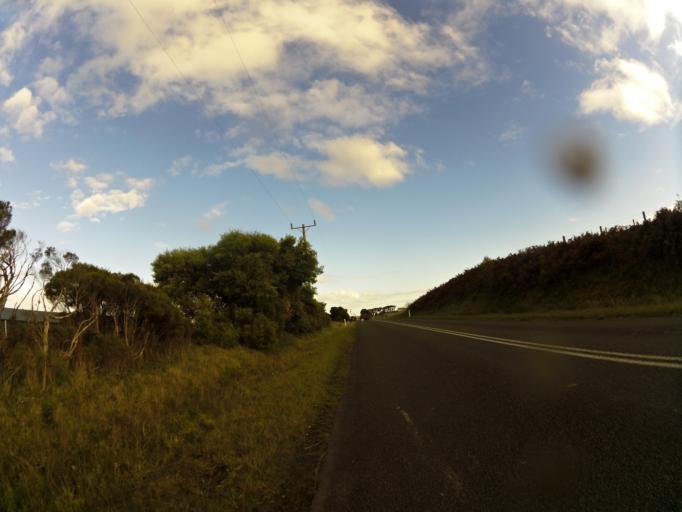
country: AU
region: Victoria
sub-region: Bass Coast
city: North Wonthaggi
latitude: -38.5524
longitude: 145.5497
